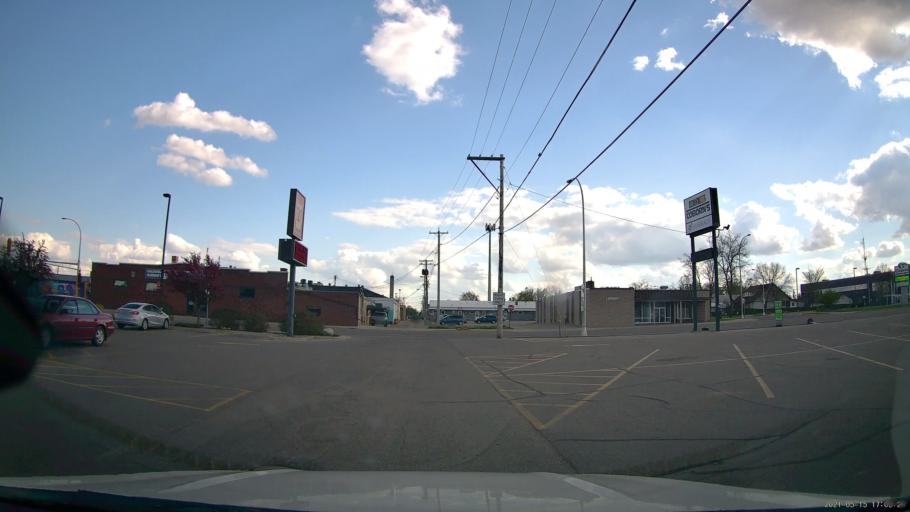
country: US
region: Minnesota
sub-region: Hubbard County
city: Park Rapids
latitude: 46.9226
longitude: -95.0609
